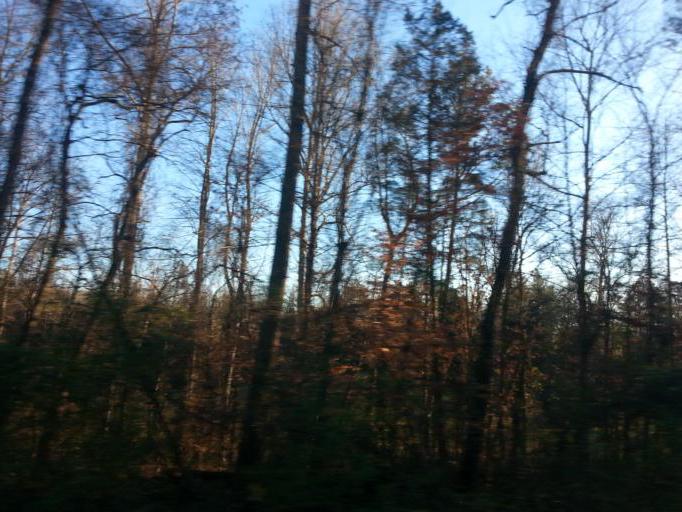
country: US
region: Tennessee
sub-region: Anderson County
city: Norris
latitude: 36.1825
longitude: -84.0772
